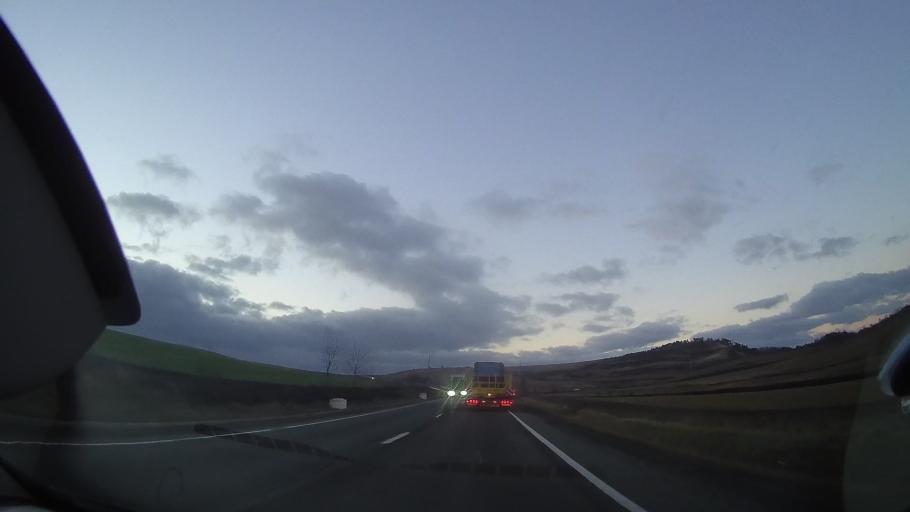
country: RO
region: Cluj
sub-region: Comuna Izvoru Crisului
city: Izvoru Crisului
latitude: 46.8198
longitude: 23.1710
